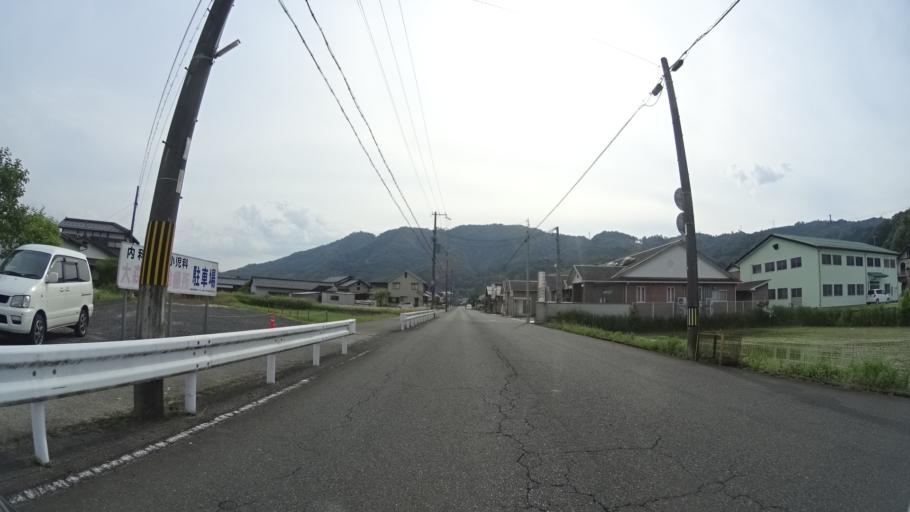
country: JP
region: Kyoto
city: Miyazu
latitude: 35.5621
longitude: 135.1487
